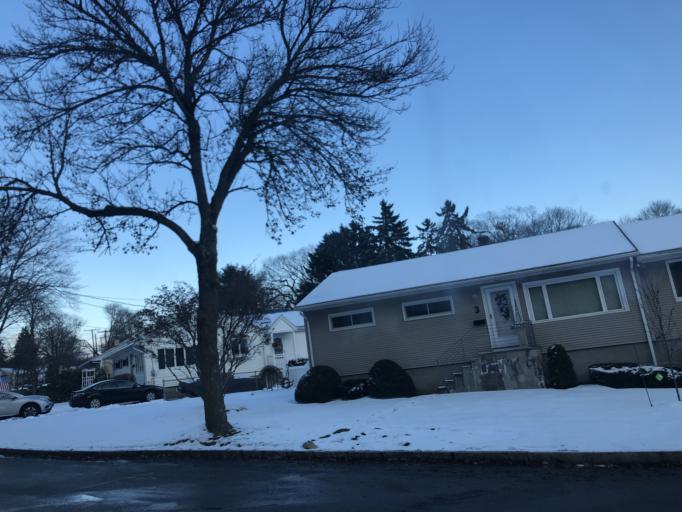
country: US
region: Massachusetts
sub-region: Middlesex County
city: Arlington
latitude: 42.4265
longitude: -71.1654
